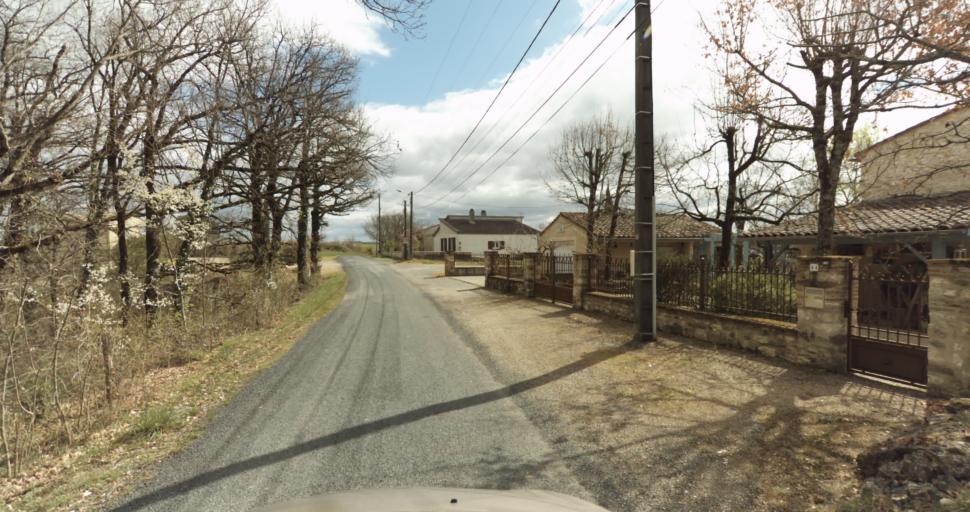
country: FR
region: Midi-Pyrenees
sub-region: Departement du Tarn
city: Puygouzon
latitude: 43.8831
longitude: 2.1516
